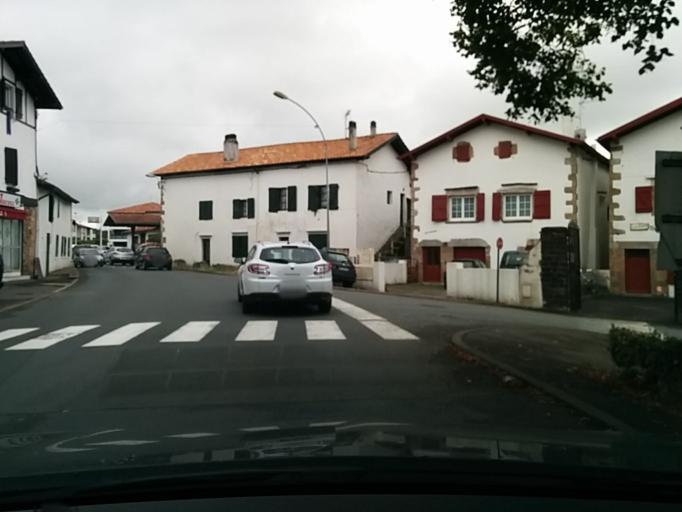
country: FR
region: Aquitaine
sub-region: Departement des Pyrenees-Atlantiques
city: Saint-Pee-sur-Nivelle
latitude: 43.3559
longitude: -1.5685
